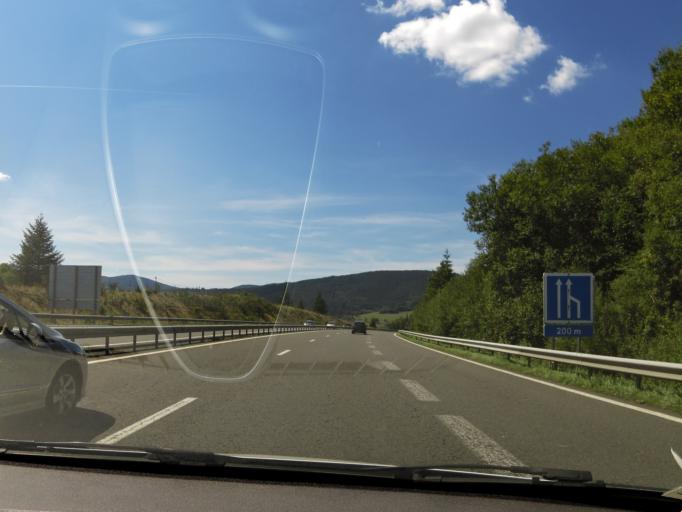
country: FR
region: Rhone-Alpes
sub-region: Departement de la Loire
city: Noiretable
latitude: 45.8483
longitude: 3.7632
